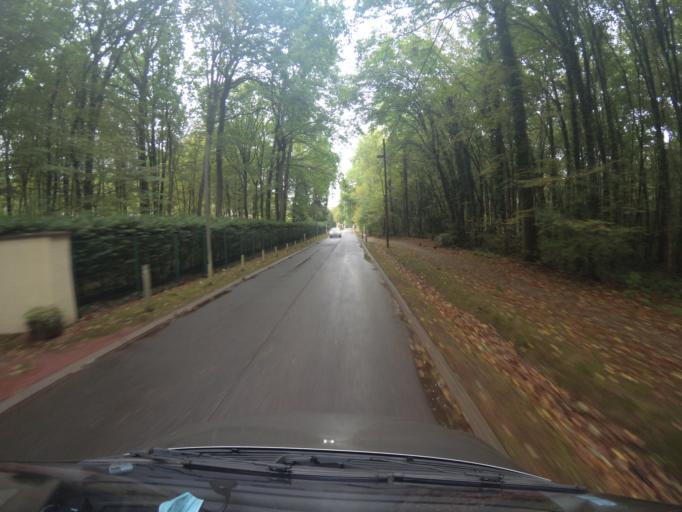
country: FR
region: Ile-de-France
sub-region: Departement de Seine-et-Marne
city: Chanteloup-en-Brie
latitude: 48.8646
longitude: 2.7327
